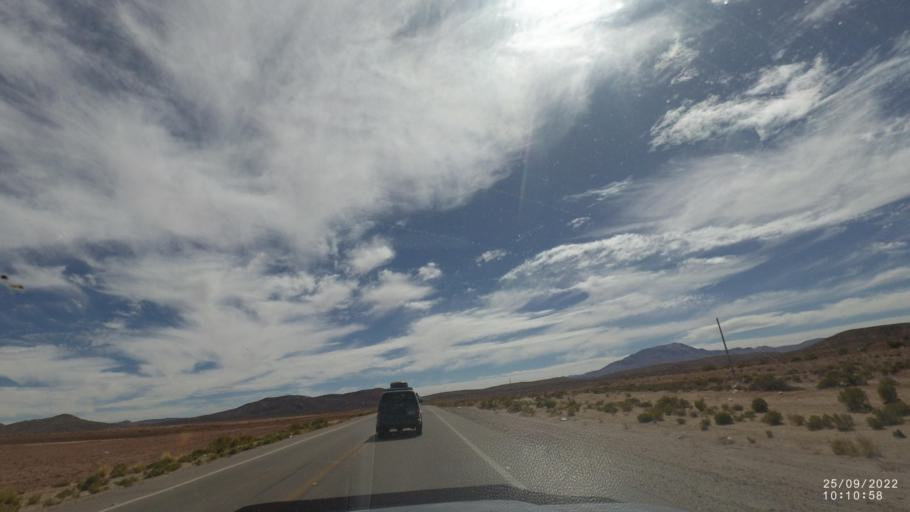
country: BO
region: Potosi
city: Colchani
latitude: -20.1065
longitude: -66.9080
